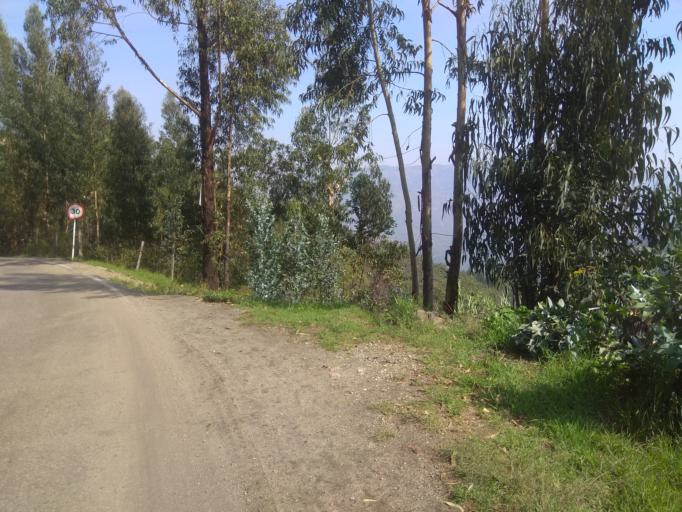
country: CO
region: Boyaca
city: Socha Viejo
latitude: 5.9787
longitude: -72.7051
